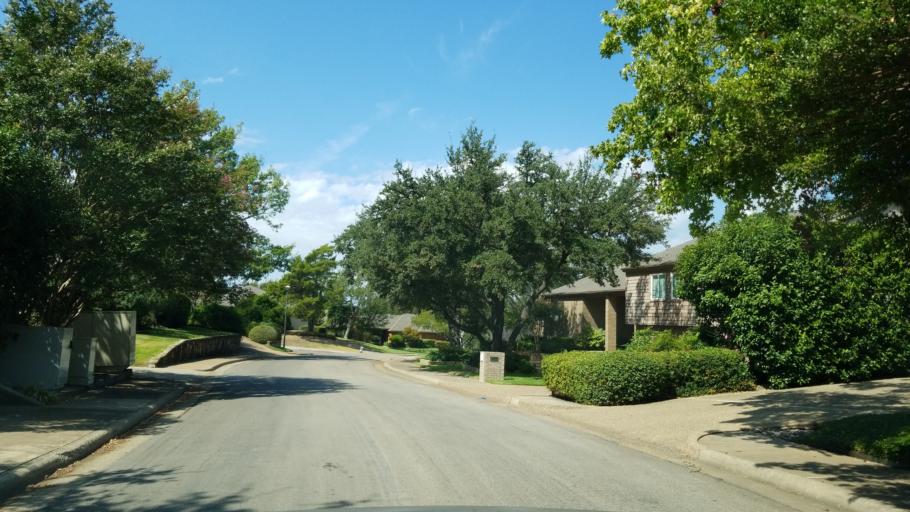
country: US
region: Texas
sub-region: Dallas County
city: Addison
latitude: 32.9634
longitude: -96.8028
